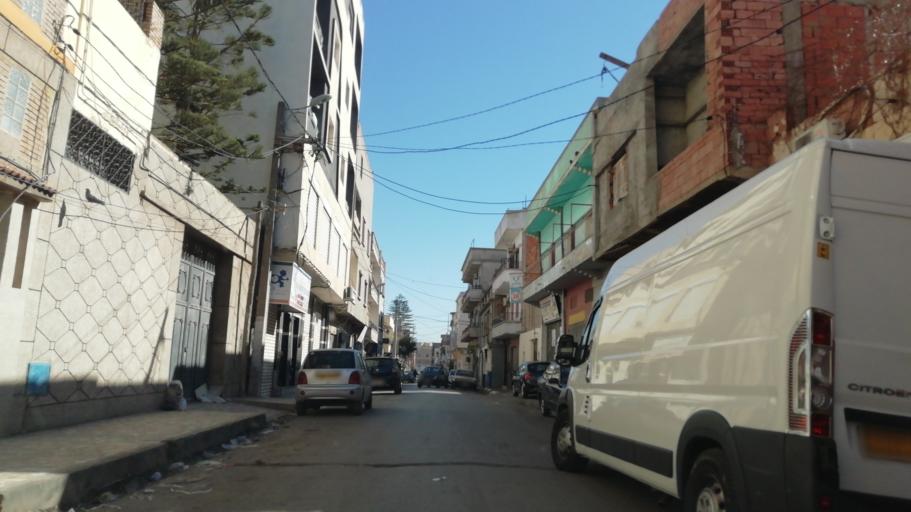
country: DZ
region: Oran
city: Oran
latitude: 35.6943
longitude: -0.6238
